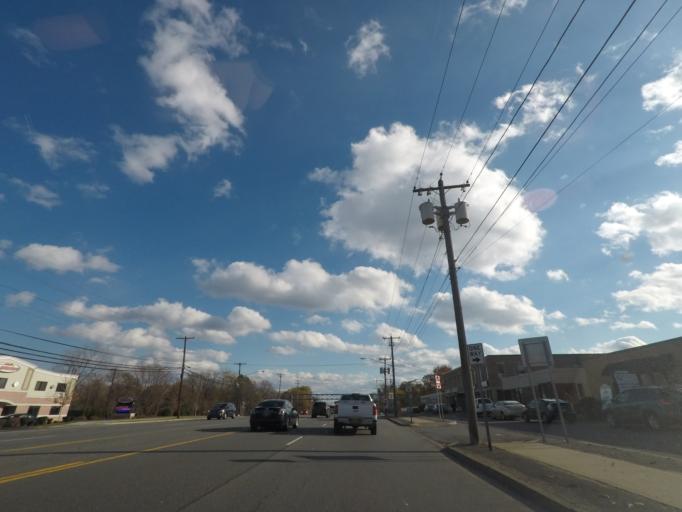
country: US
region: New York
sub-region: Albany County
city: Colonie
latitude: 42.7134
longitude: -73.8282
